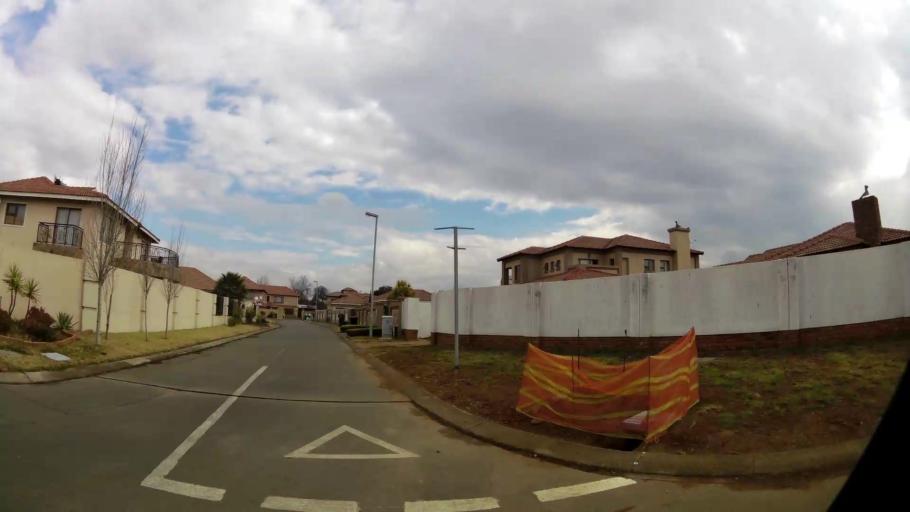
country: ZA
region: Gauteng
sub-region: Sedibeng District Municipality
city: Vanderbijlpark
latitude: -26.7248
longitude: 27.8643
